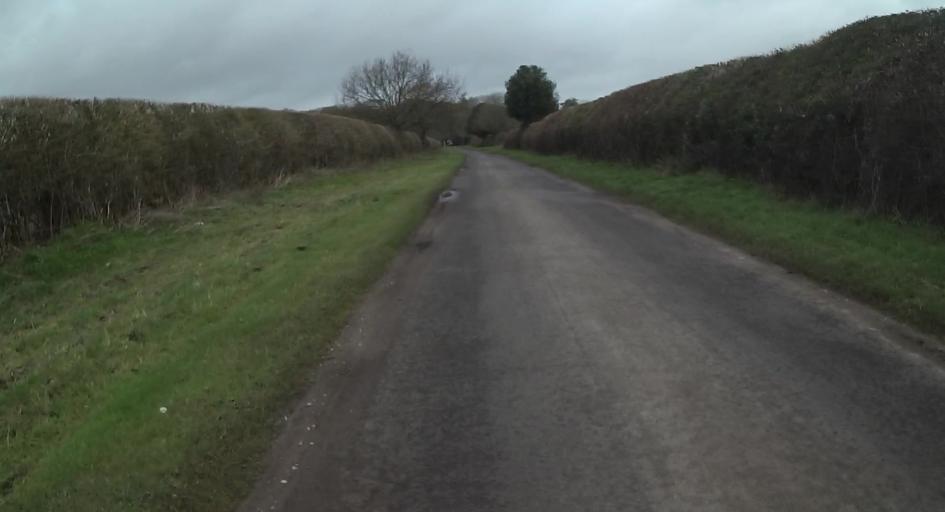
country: GB
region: England
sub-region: Hampshire
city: Overton
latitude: 51.2722
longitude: -1.2003
